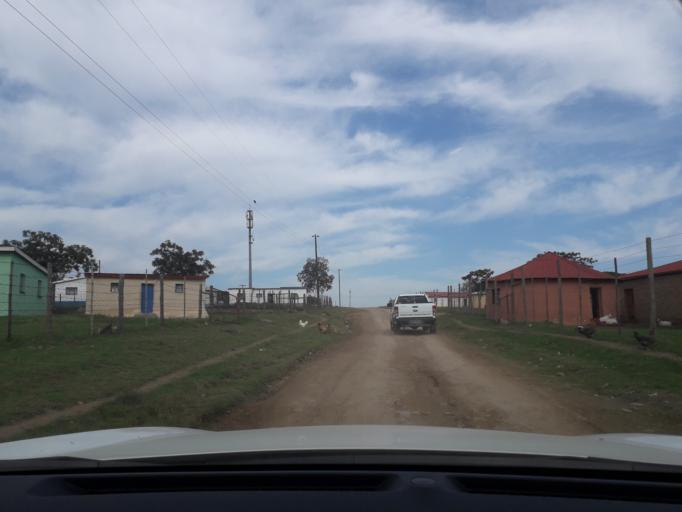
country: ZA
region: Eastern Cape
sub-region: Buffalo City Metropolitan Municipality
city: Bhisho
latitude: -32.9908
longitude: 27.3580
